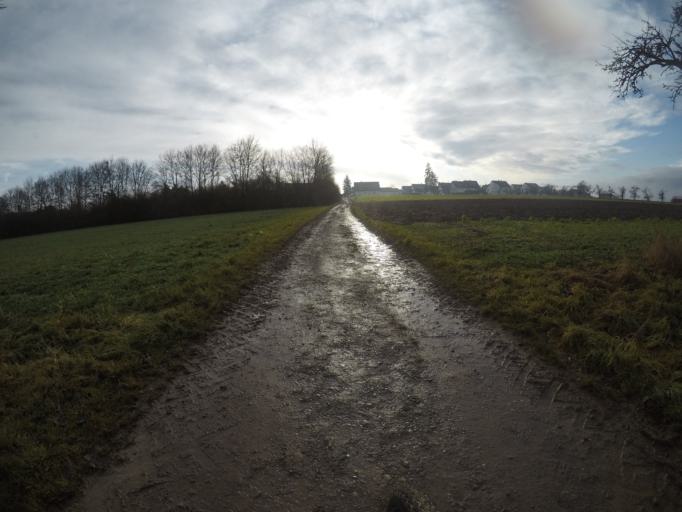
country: DE
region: Baden-Wuerttemberg
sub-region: Regierungsbezirk Stuttgart
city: Herrenberg
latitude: 48.6160
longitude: 8.8371
